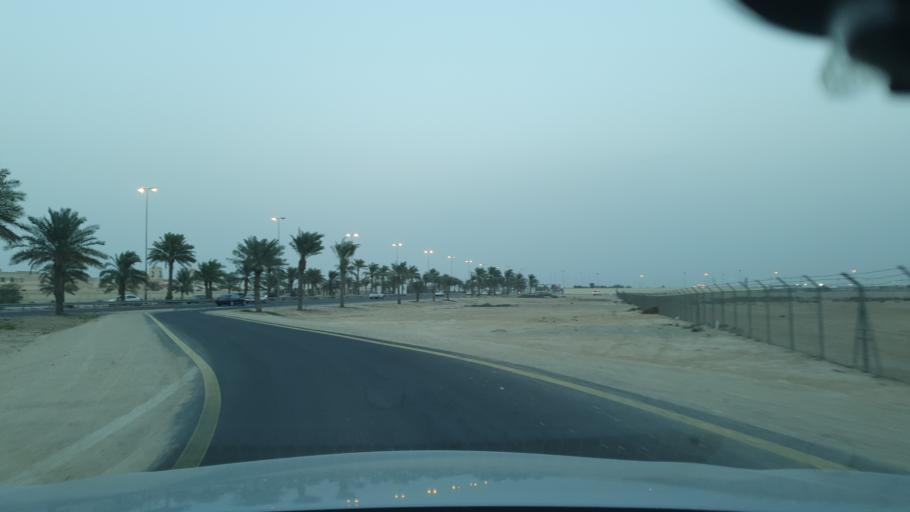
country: BH
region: Northern
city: Ar Rifa'
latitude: 26.0988
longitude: 50.5496
